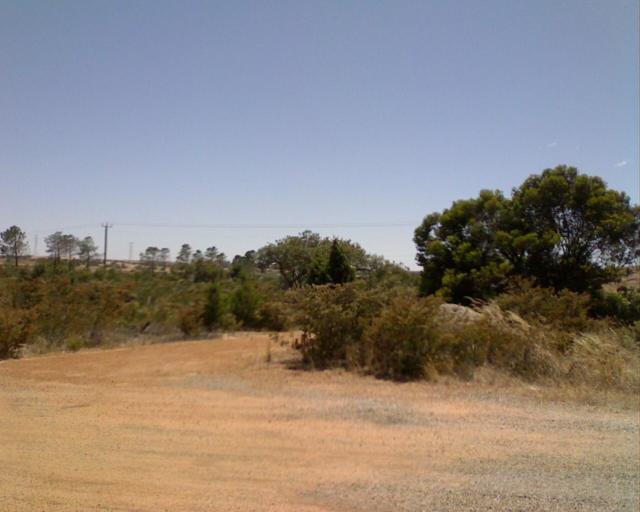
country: AU
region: Western Australia
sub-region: Dandaragan
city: Jurien Bay
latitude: -30.0565
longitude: 115.3303
